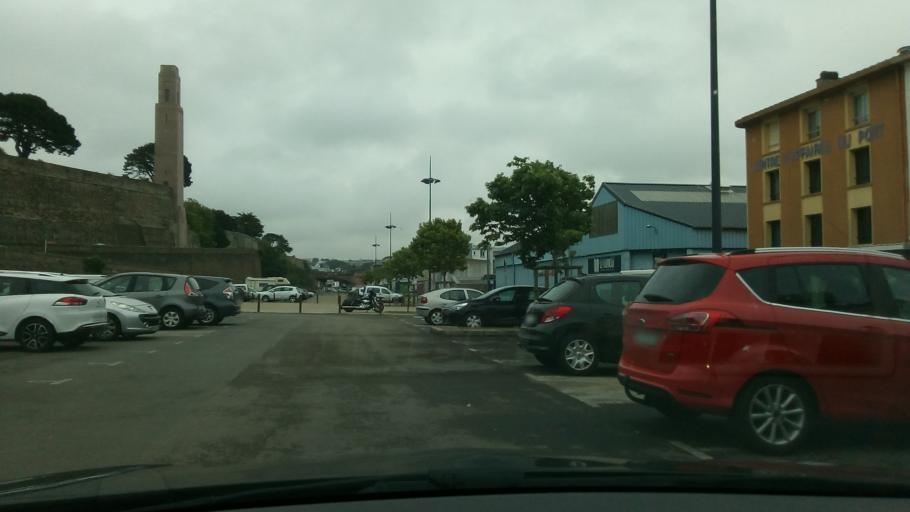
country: FR
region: Brittany
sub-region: Departement du Finistere
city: Brest
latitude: 48.3823
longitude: -4.4884
